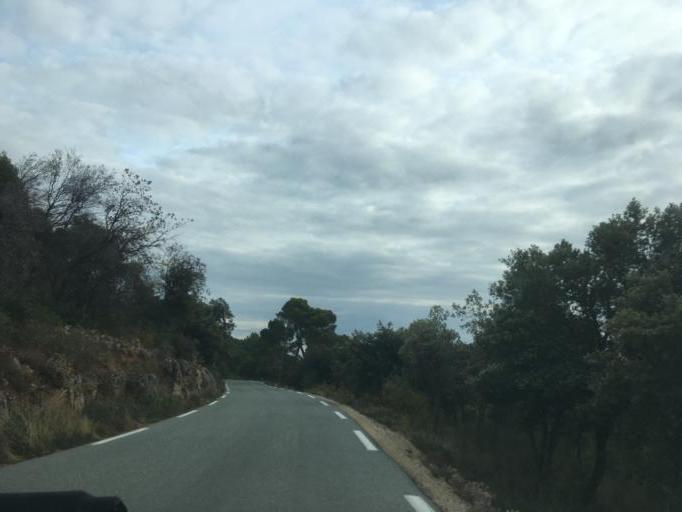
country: FR
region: Provence-Alpes-Cote d'Azur
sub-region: Departement du Var
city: Villecroze
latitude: 43.5804
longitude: 6.3111
